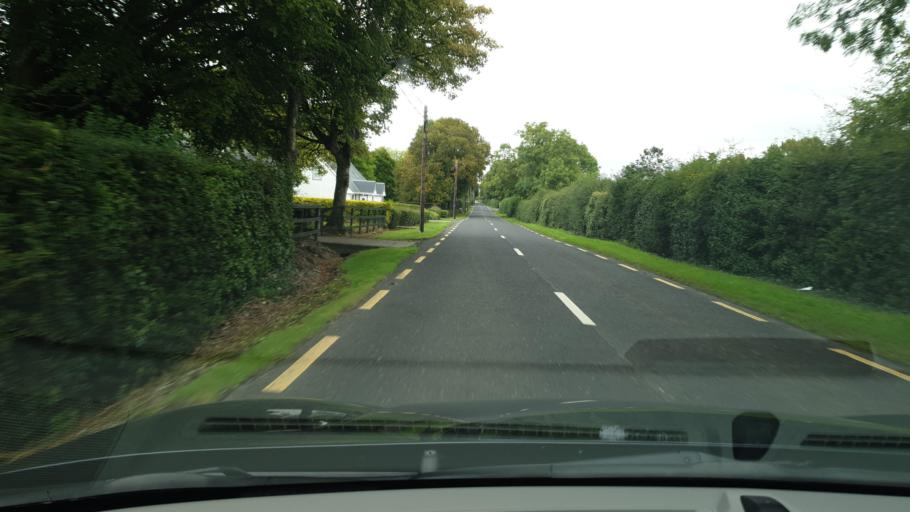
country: IE
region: Leinster
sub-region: Kildare
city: Maynooth
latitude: 53.3574
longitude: -6.6360
